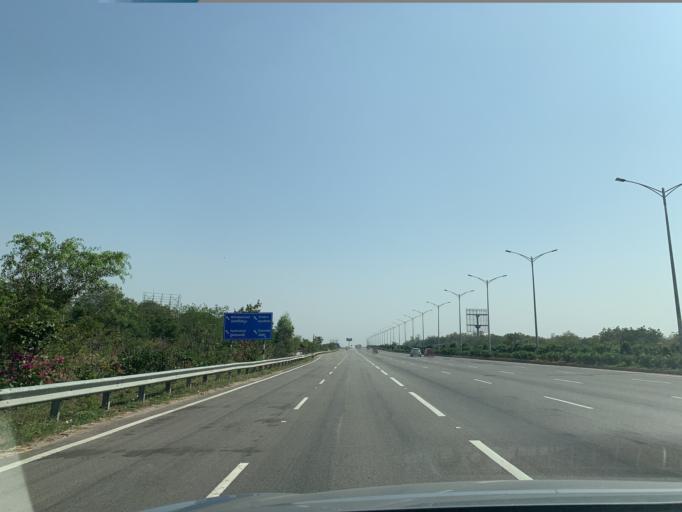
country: IN
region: Telangana
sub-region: Hyderabad
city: Hyderabad
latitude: 17.3565
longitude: 78.3565
